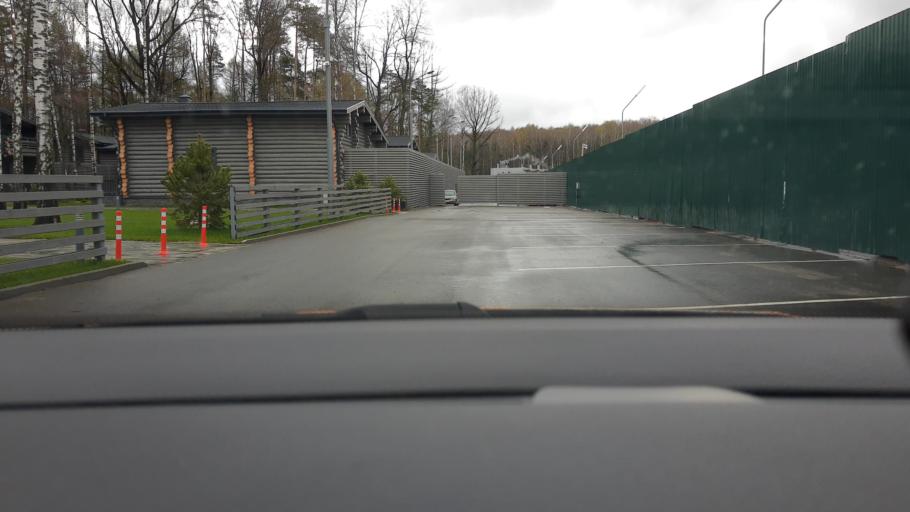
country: RU
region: Moscow
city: Lianozovo
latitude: 55.9099
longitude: 37.5965
